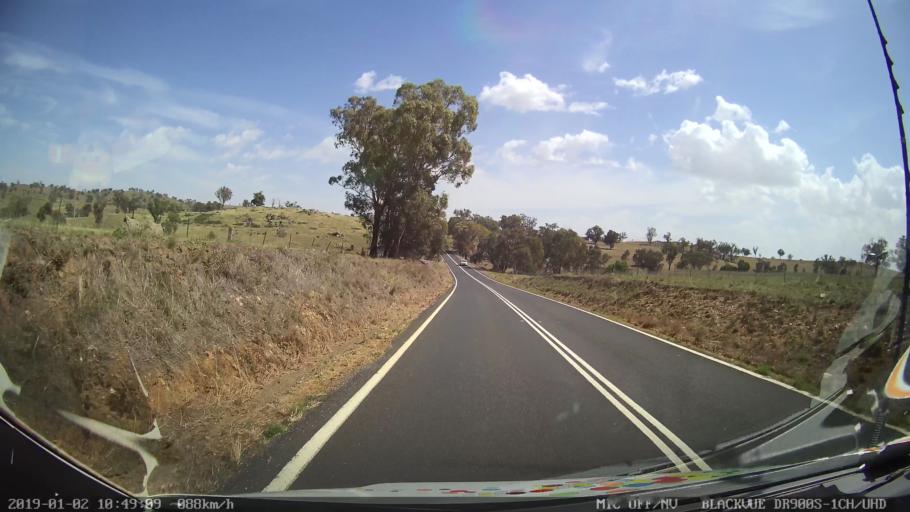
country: AU
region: New South Wales
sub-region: Cootamundra
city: Cootamundra
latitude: -34.7282
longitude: 148.2776
